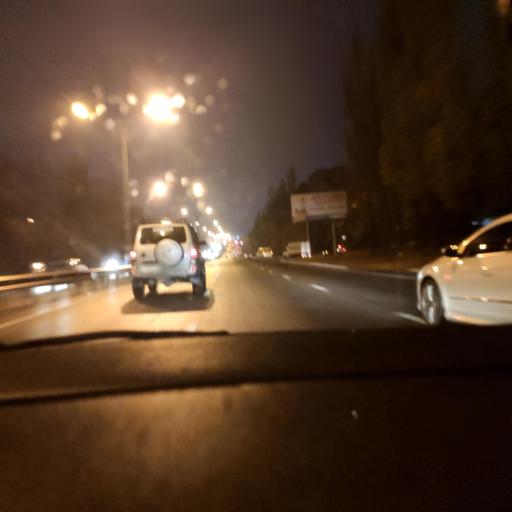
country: RU
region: Voronezj
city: Voronezh
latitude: 51.6618
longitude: 39.1304
